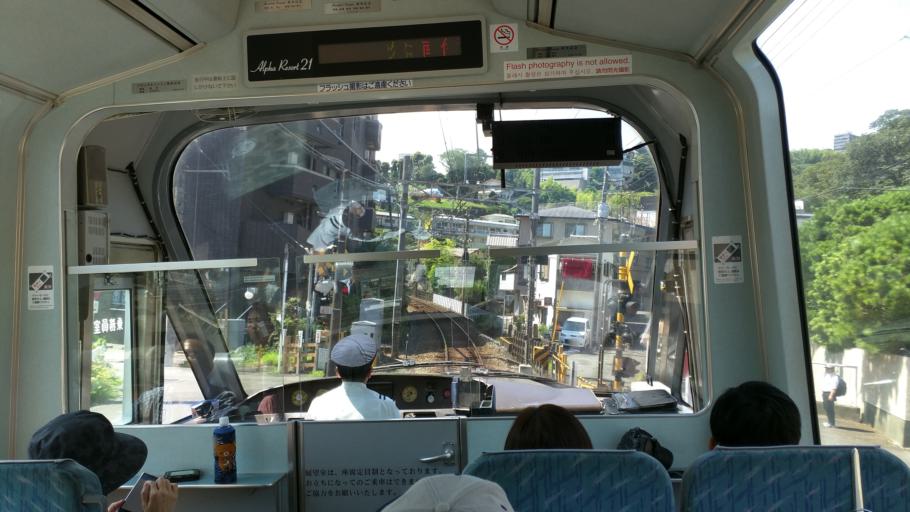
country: JP
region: Shizuoka
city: Ito
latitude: 34.9689
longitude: 139.0893
